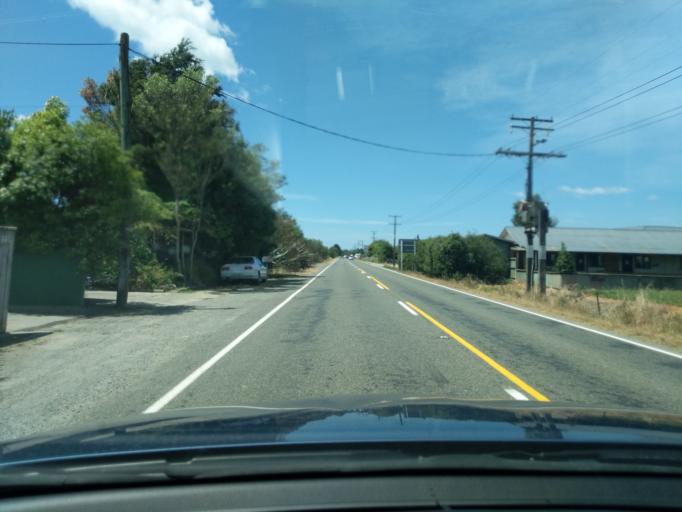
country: NZ
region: Tasman
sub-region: Tasman District
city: Motueka
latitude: -41.0698
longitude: 172.9866
